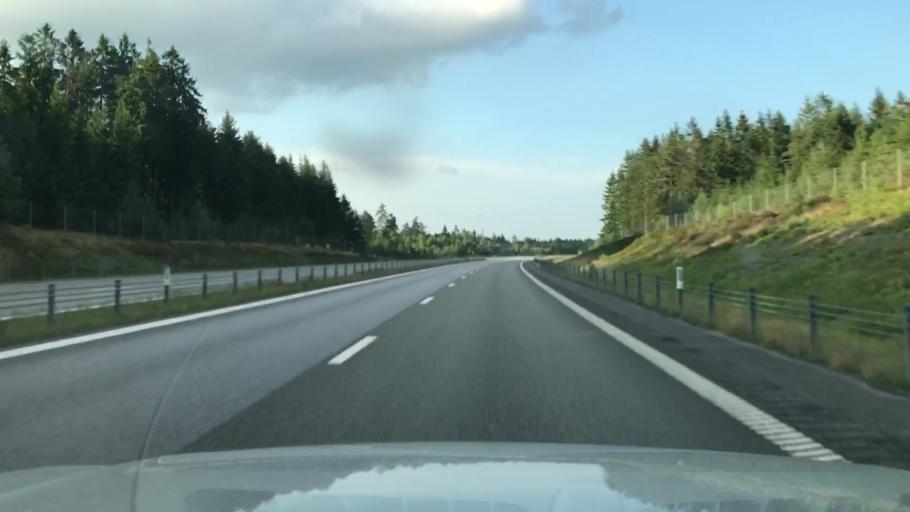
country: SE
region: Kronoberg
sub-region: Markaryds Kommun
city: Markaryd
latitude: 56.4193
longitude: 13.5509
